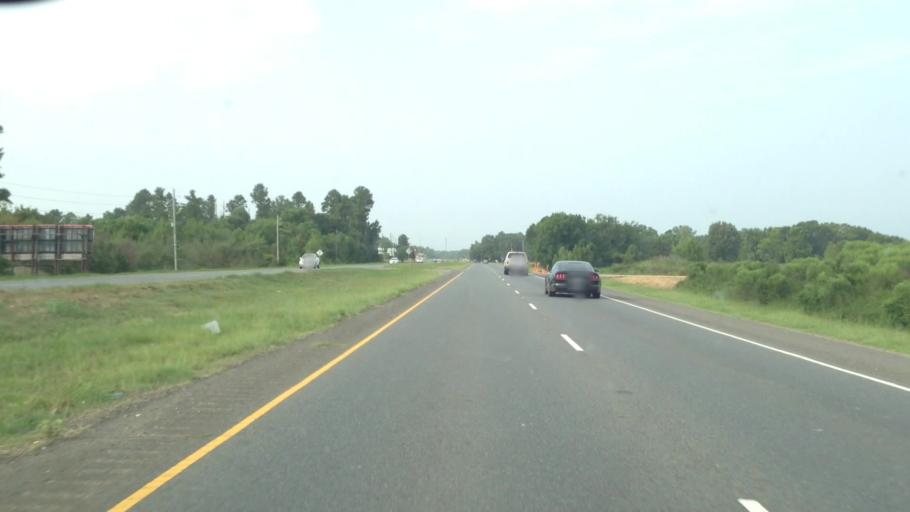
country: US
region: Louisiana
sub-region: De Soto Parish
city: Stonewall
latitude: 32.3757
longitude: -93.8218
